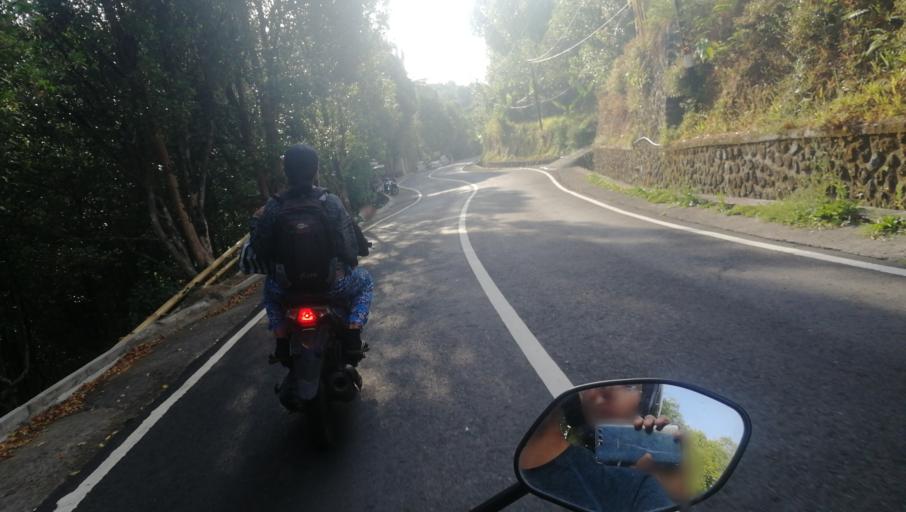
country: ID
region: Bali
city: Munduk
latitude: -8.2632
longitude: 115.0642
